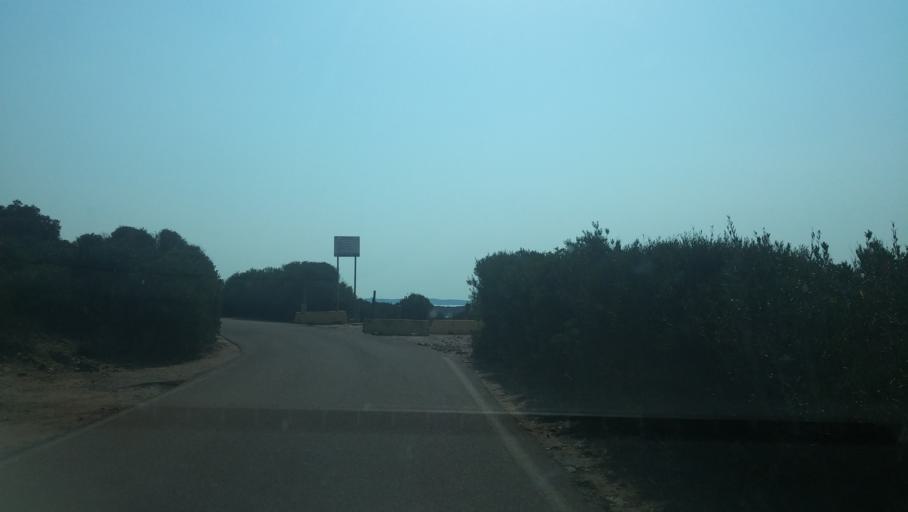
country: IT
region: Sardinia
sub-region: Provincia di Olbia-Tempio
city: La Maddalena
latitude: 41.1830
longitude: 9.4587
